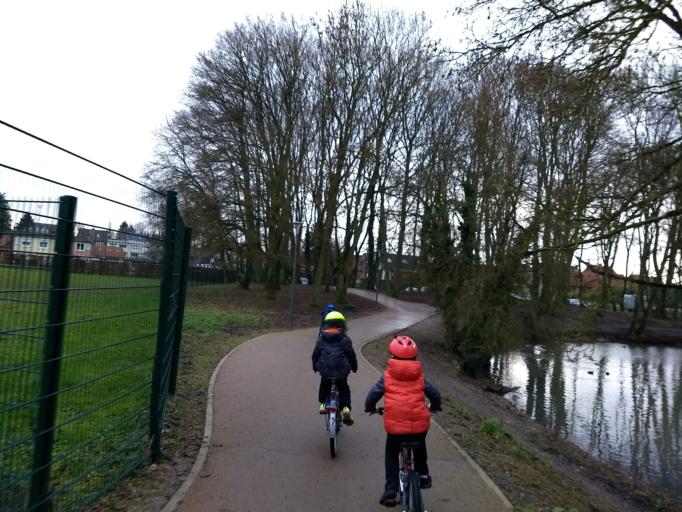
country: FR
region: Nord-Pas-de-Calais
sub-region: Departement du Pas-de-Calais
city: Achicourt
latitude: 50.2820
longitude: 2.7648
